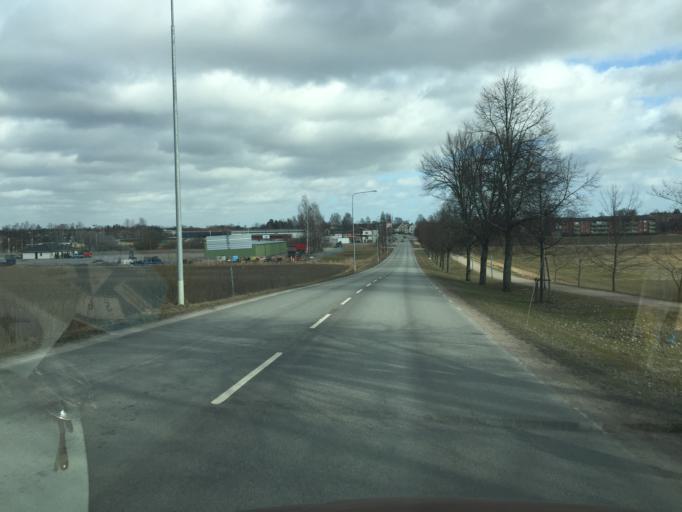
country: SE
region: Soedermanland
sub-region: Vingakers Kommun
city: Vingaker
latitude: 59.0370
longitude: 15.8616
